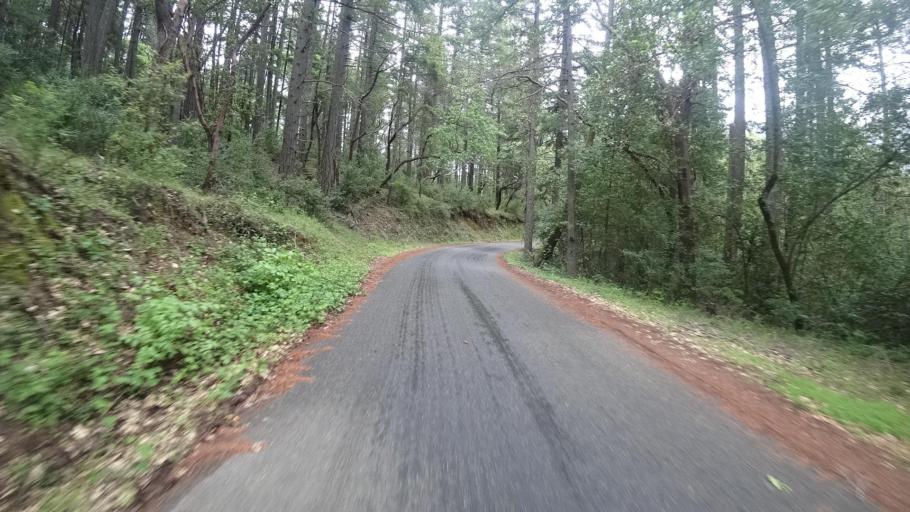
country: US
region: California
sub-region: Siskiyou County
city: Happy Camp
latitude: 41.3721
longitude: -123.5004
